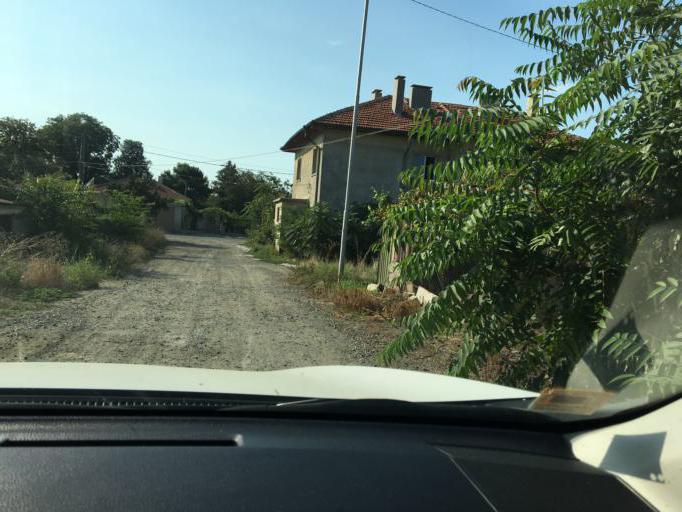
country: BG
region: Burgas
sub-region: Obshtina Burgas
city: Burgas
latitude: 42.6117
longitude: 27.4856
